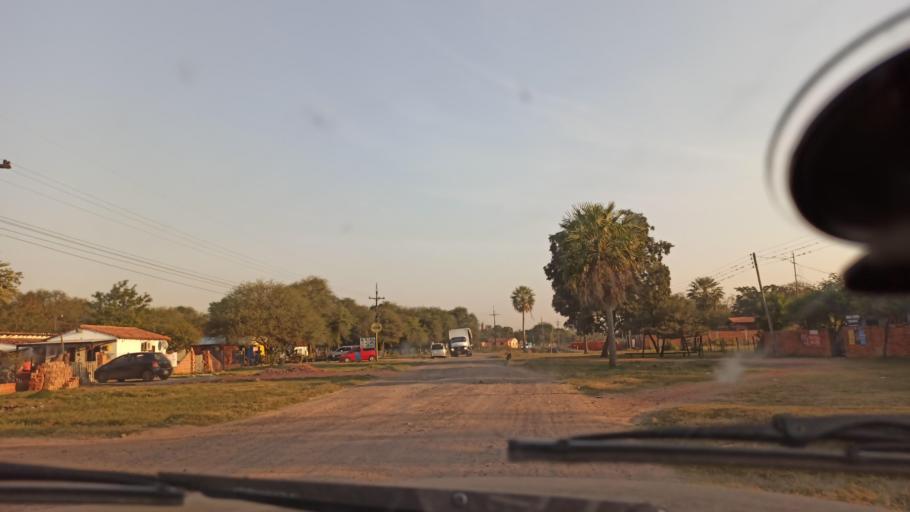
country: PY
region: Presidente Hayes
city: Nanawa
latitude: -25.2334
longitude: -57.6314
